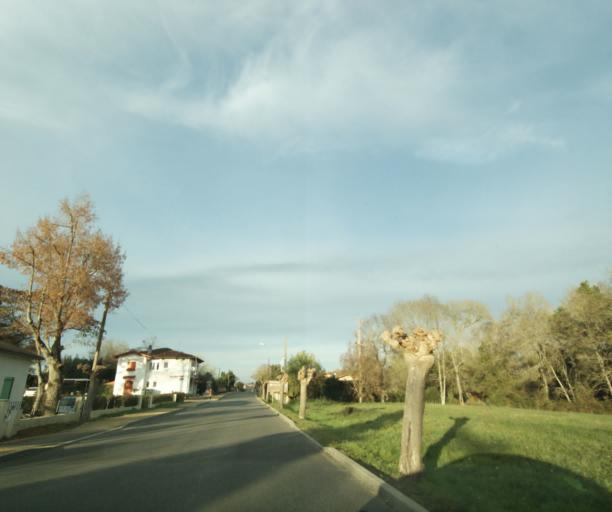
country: FR
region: Aquitaine
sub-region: Departement des Landes
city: Gabarret
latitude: 43.9794
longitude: 0.0076
